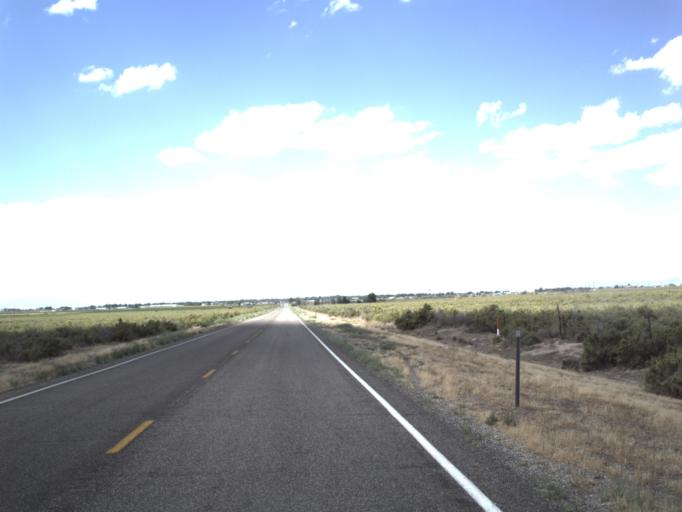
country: US
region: Utah
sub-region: Millard County
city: Delta
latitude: 39.3532
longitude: -112.5128
